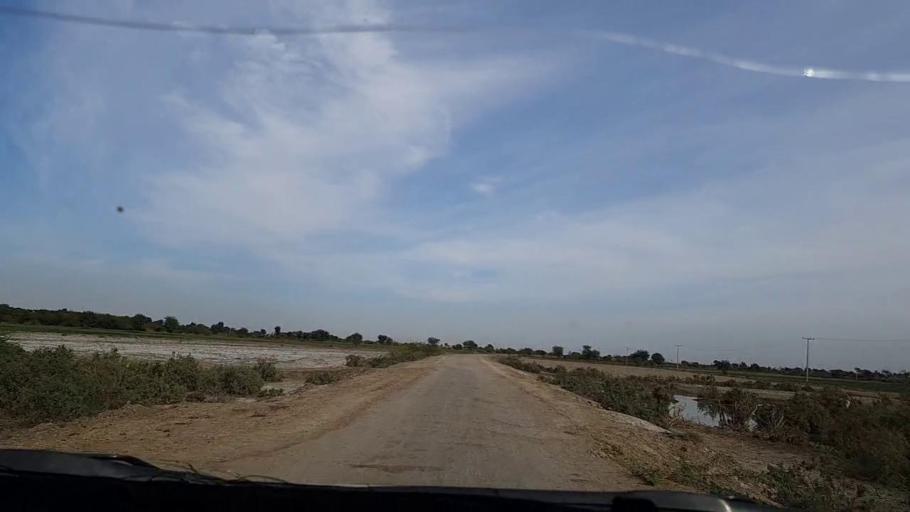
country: PK
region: Sindh
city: Dhoro Naro
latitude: 25.4750
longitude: 69.5292
